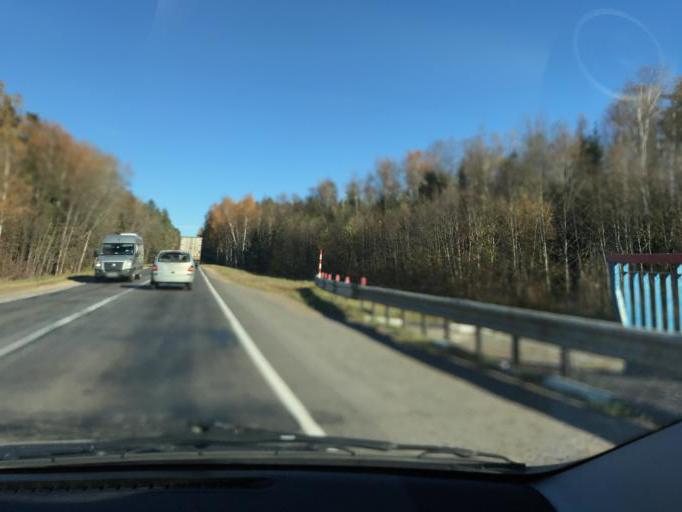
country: BY
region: Vitebsk
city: Polatsk
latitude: 55.3370
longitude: 28.7911
